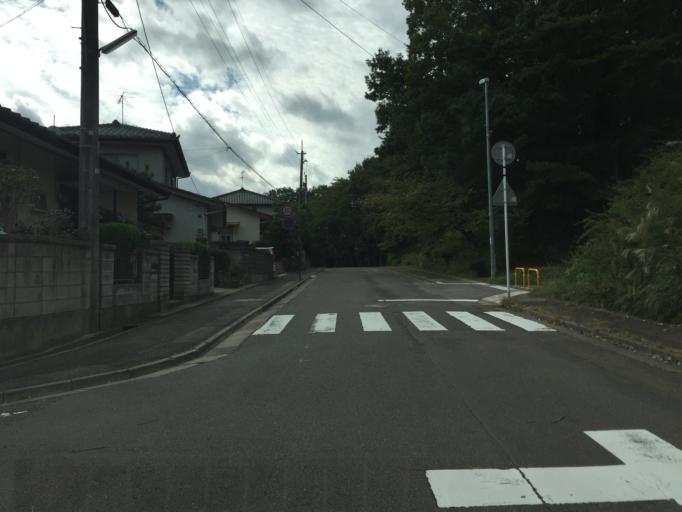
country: JP
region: Fukushima
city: Fukushima-shi
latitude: 37.7009
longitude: 140.4661
